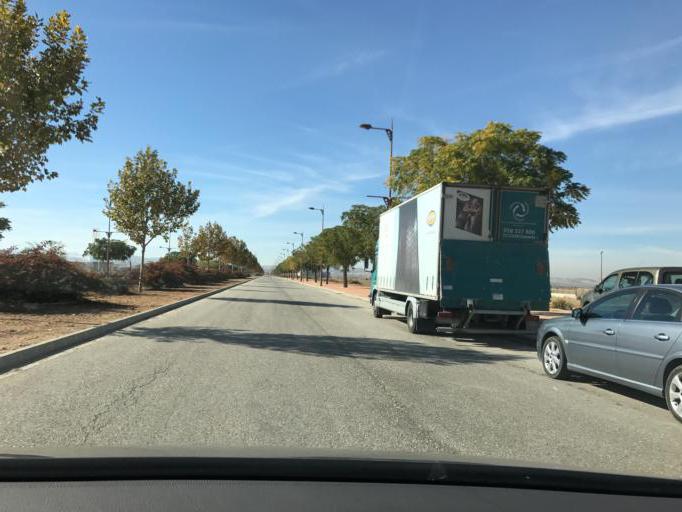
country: ES
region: Andalusia
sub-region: Provincia de Granada
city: Escuzar
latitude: 37.0848
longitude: -3.7649
